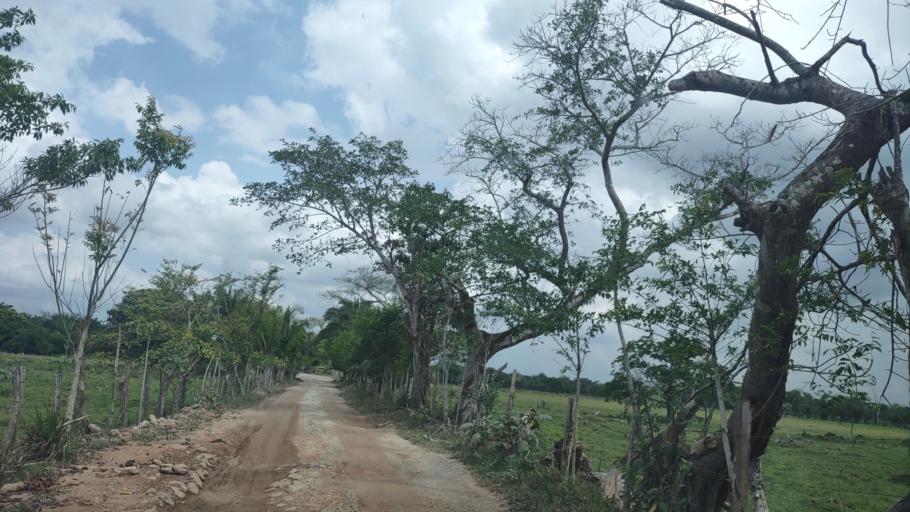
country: MX
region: Veracruz
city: Las Choapas
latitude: 17.9611
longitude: -94.1213
